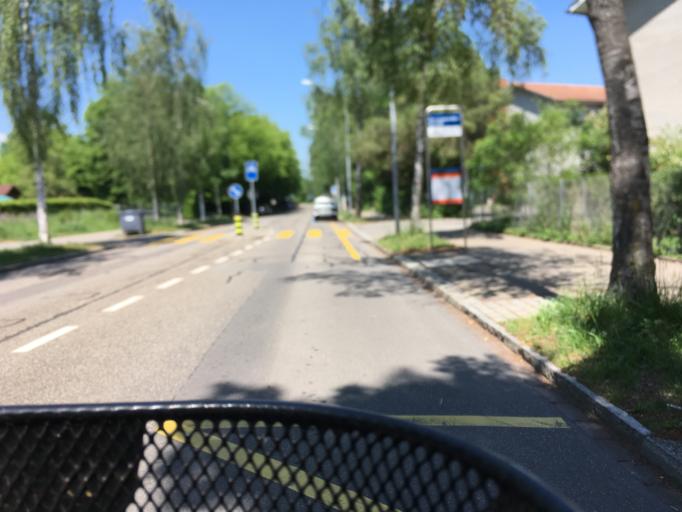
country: CH
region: Zurich
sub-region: Bezirk Zuerich
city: Zuerich (Kreis 12) / Schwamendingen-Mitte
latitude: 47.4074
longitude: 8.5728
